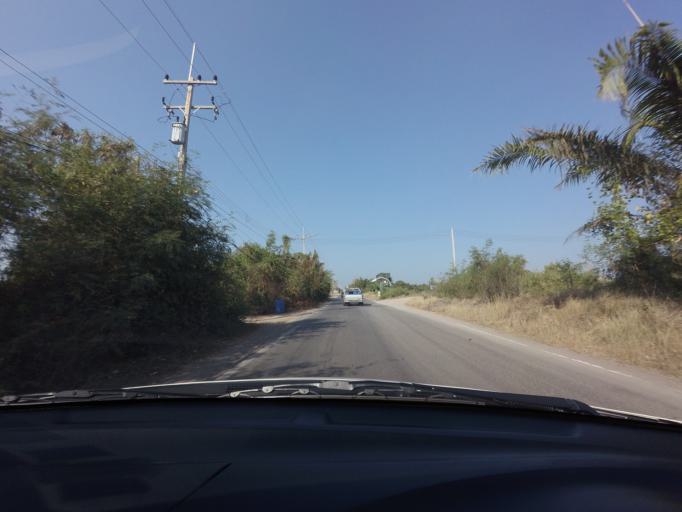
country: TH
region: Samut Sakhon
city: Ban Phaeo
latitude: 13.5040
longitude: 100.0885
